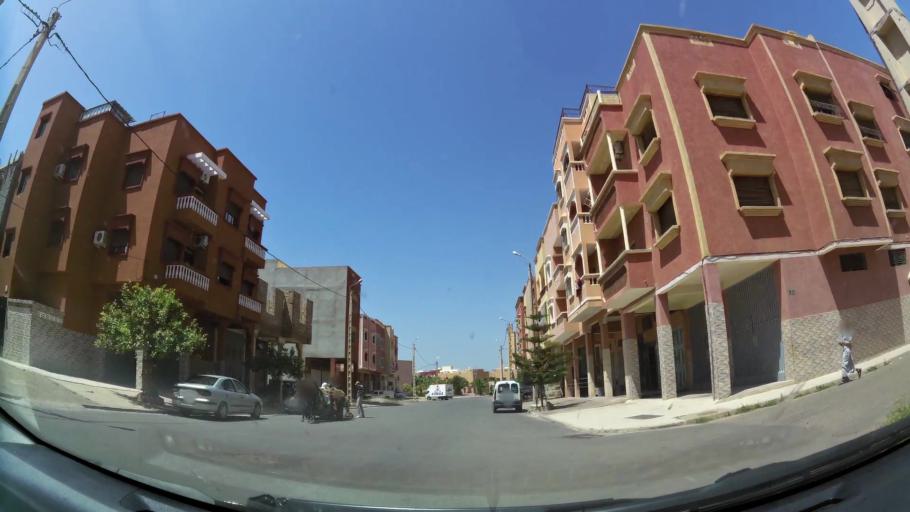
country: MA
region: Souss-Massa-Draa
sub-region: Inezgane-Ait Mellou
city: Inezgane
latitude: 30.3486
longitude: -9.4842
